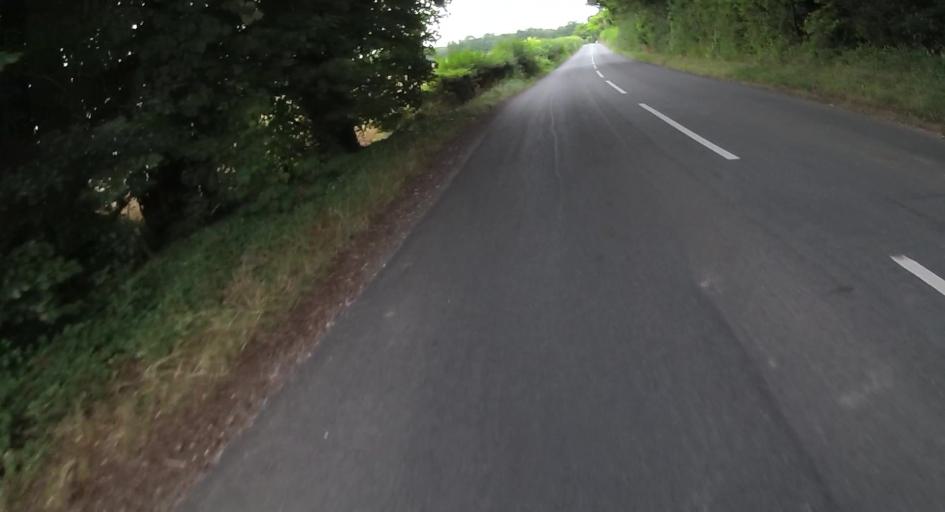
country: GB
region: England
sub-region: Hampshire
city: Kings Worthy
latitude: 51.1177
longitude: -1.3097
